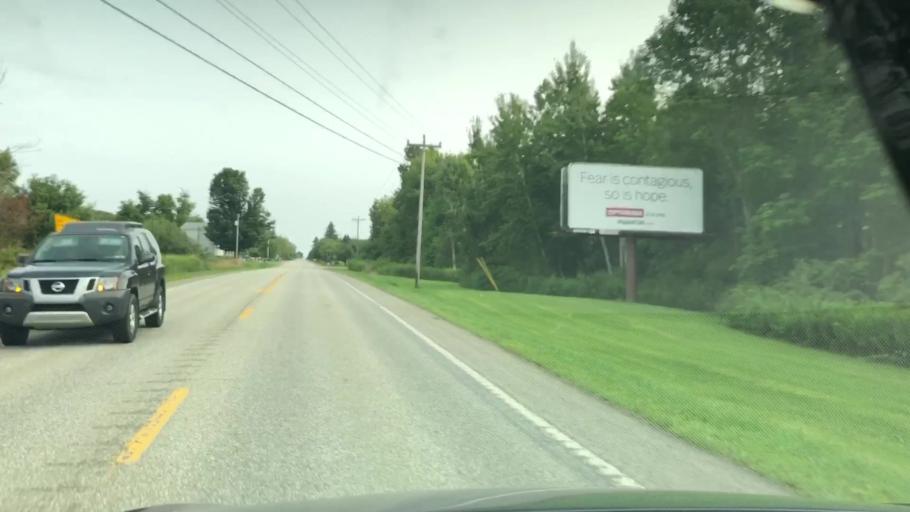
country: US
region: Pennsylvania
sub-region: Erie County
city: Union City
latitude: 41.8822
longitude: -79.8436
